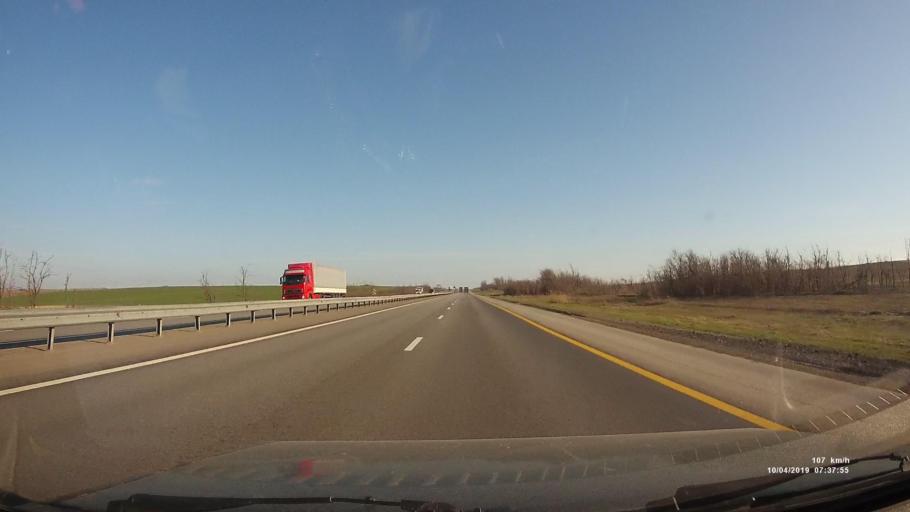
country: RU
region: Rostov
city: Likhoy
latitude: 48.0807
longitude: 40.2596
